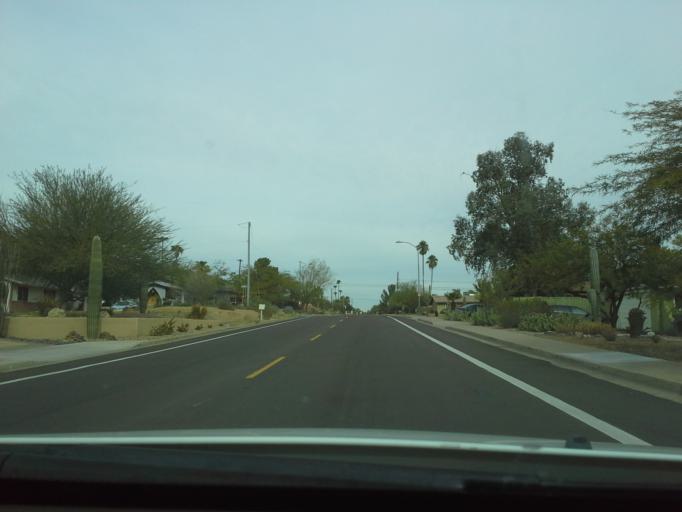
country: US
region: Arizona
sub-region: Maricopa County
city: Paradise Valley
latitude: 33.6068
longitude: -112.0219
